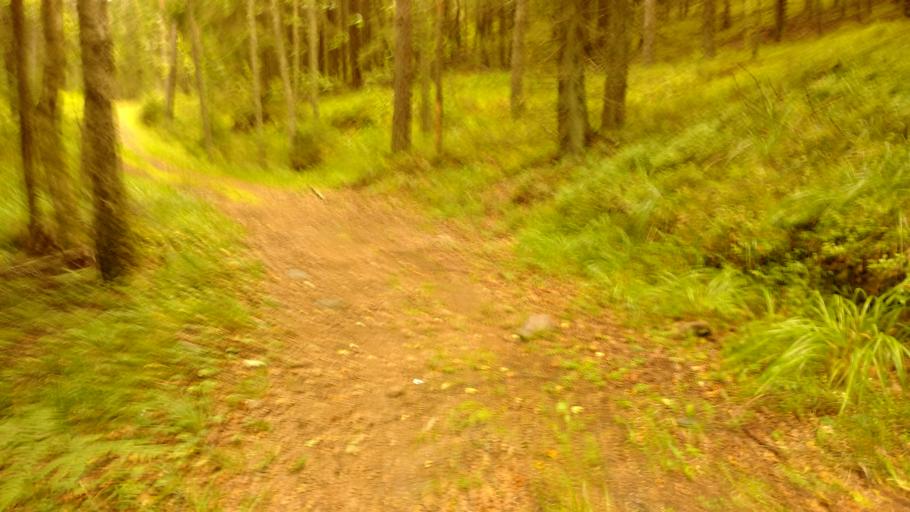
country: FI
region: Varsinais-Suomi
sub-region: Salo
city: Pertteli
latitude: 60.4020
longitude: 23.2198
